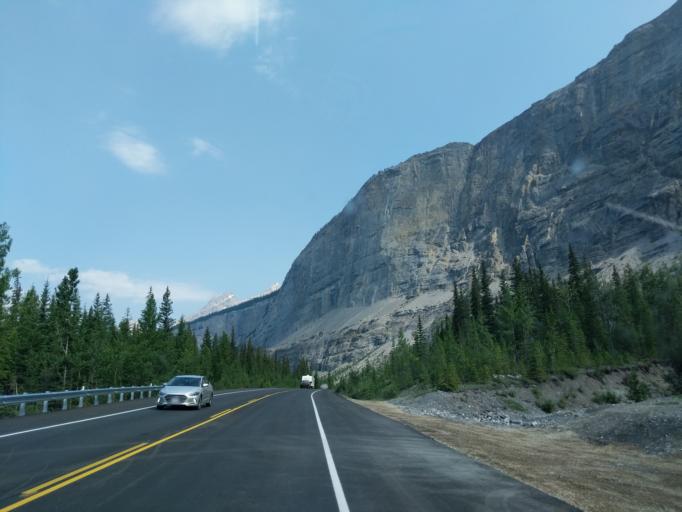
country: CA
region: British Columbia
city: Golden
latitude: 52.1356
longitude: -116.9925
